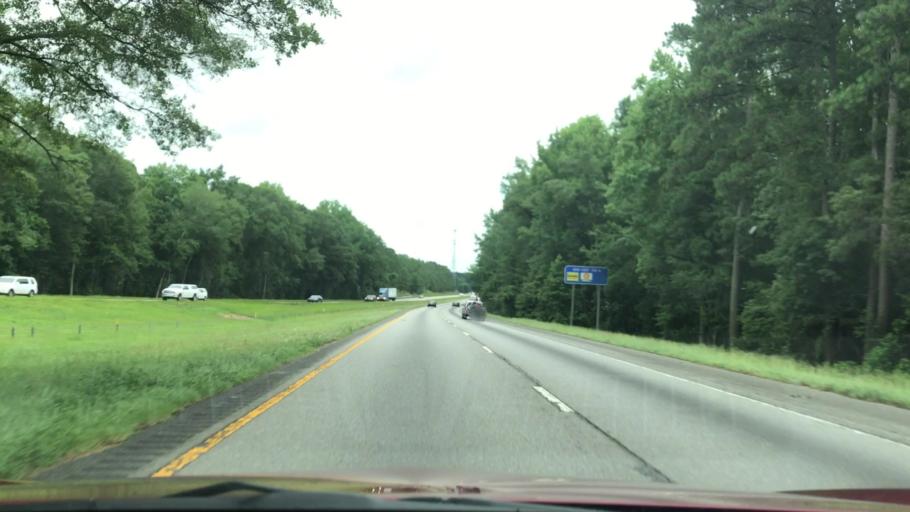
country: US
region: South Carolina
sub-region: Orangeburg County
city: Brookdale
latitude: 33.4664
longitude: -80.7412
